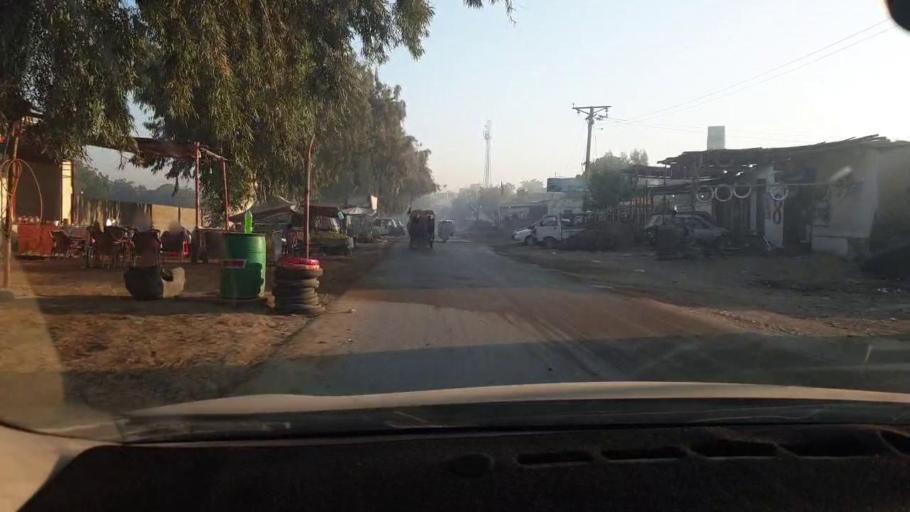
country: PK
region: Sindh
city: Malir Cantonment
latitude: 25.0075
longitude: 67.1563
